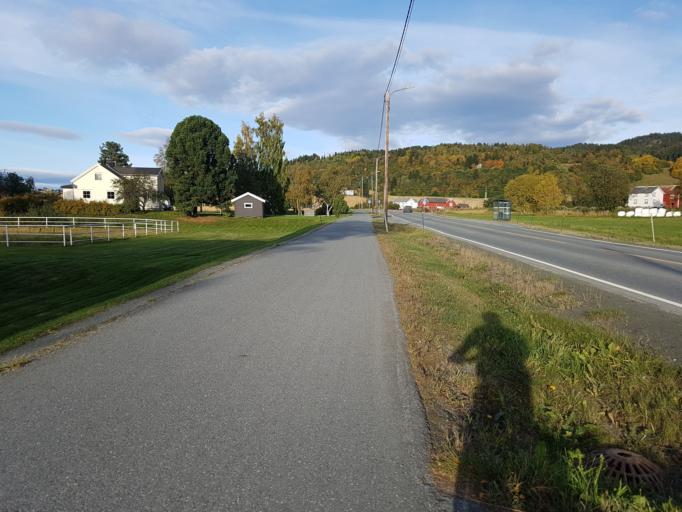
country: NO
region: Sor-Trondelag
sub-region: Trondheim
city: Trondheim
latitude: 63.3760
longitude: 10.4318
